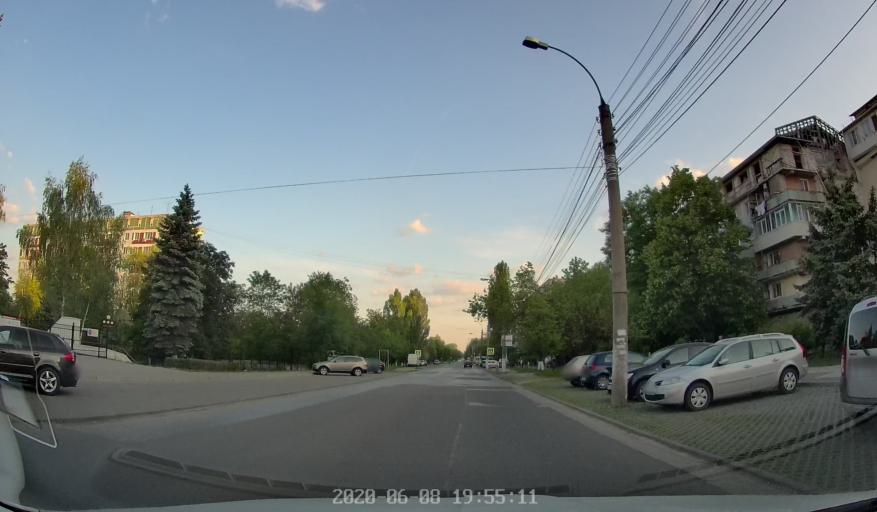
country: MD
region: Chisinau
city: Chisinau
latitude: 47.0304
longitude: 28.8840
